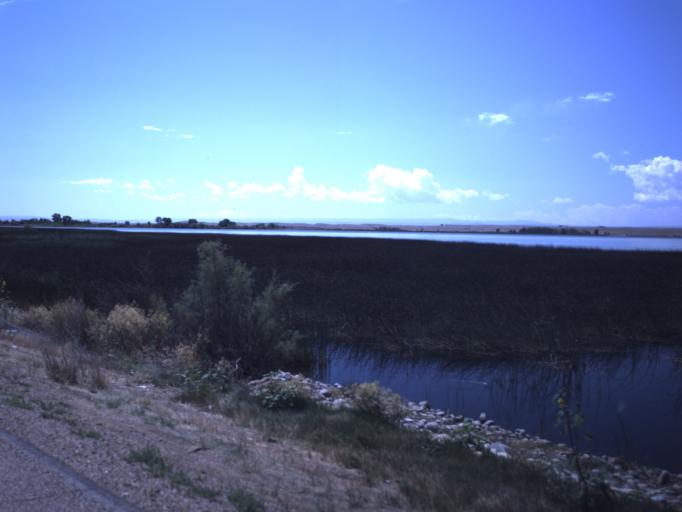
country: US
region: Utah
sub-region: Uintah County
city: Naples
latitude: 40.1994
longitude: -109.6648
